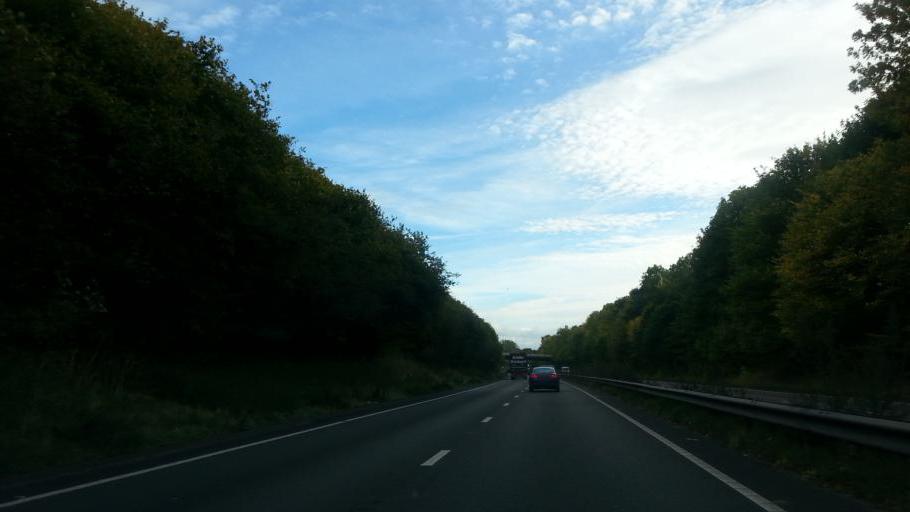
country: GB
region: England
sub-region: Nottinghamshire
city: Tuxford
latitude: 53.2395
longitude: -0.9006
